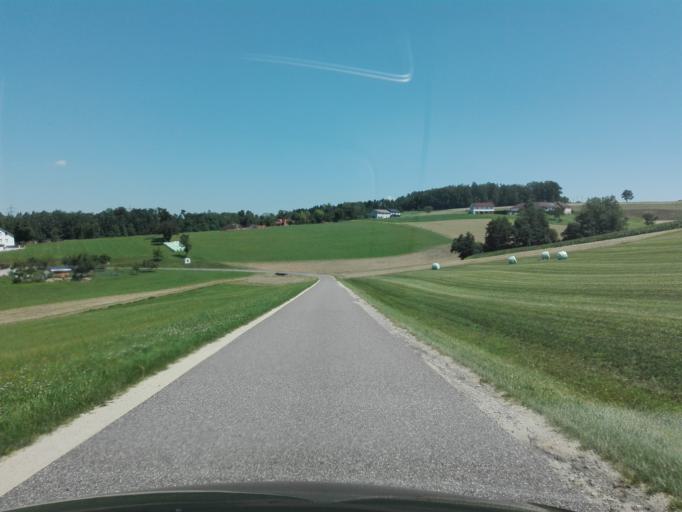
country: AT
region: Upper Austria
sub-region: Politischer Bezirk Urfahr-Umgebung
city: Gallneukirchen
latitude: 48.3161
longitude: 14.4155
